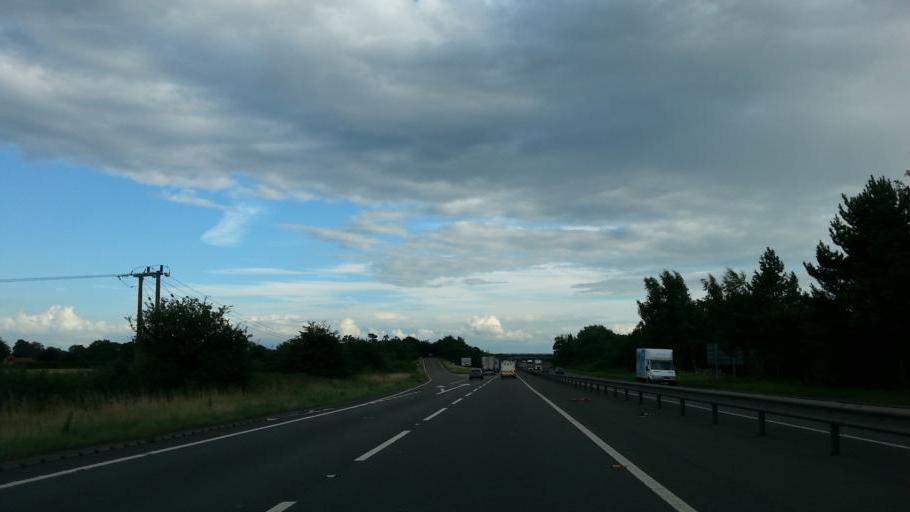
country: GB
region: England
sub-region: Nottinghamshire
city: South Collingham
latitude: 53.1726
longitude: -0.8129
